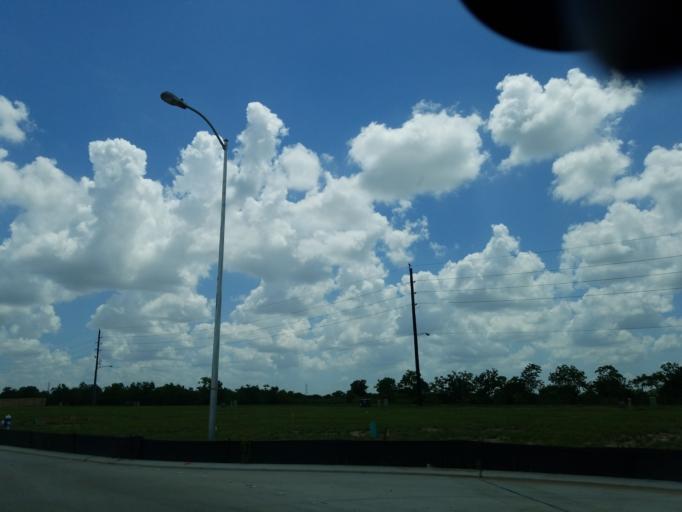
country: US
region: Texas
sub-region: Harris County
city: Katy
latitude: 29.8309
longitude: -95.7811
